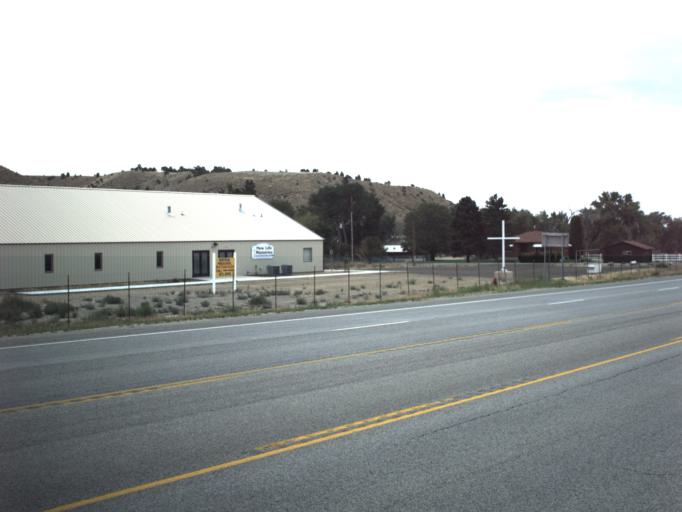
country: US
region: Utah
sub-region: Carbon County
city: Helper
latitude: 39.6770
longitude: -110.8614
